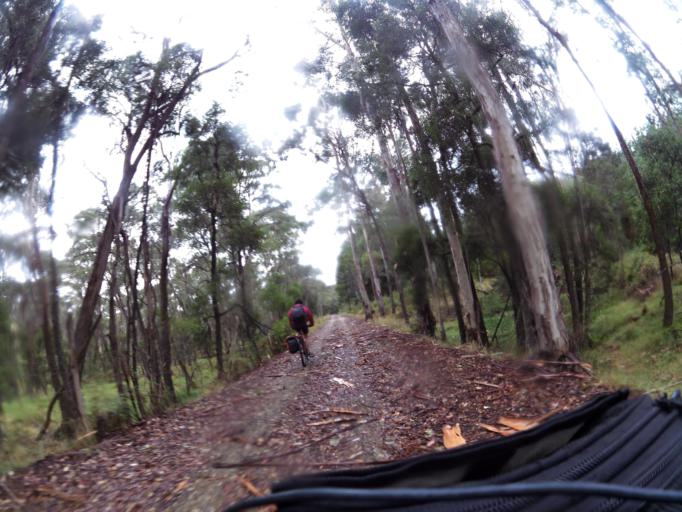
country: AU
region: New South Wales
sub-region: Greater Hume Shire
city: Holbrook
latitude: -36.1811
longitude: 147.5014
